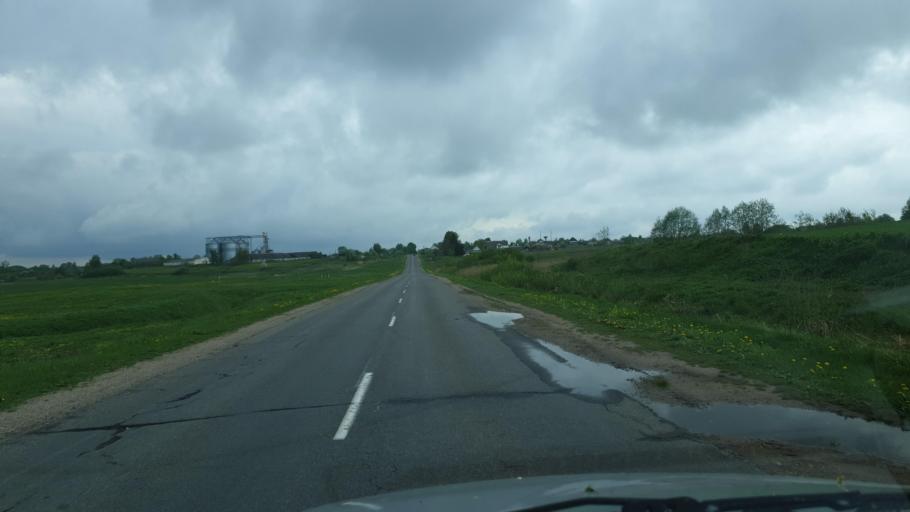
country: BY
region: Vitebsk
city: Lyepyel'
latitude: 54.8849
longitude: 28.6402
